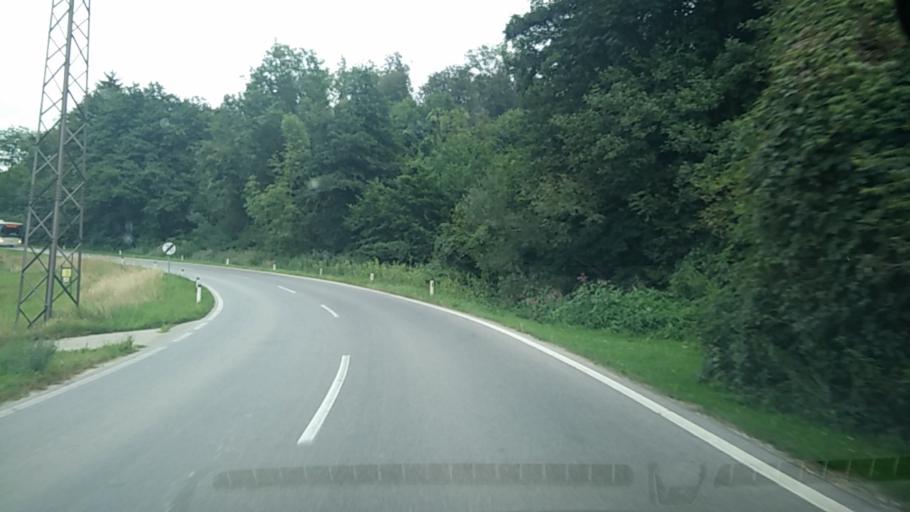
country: AT
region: Carinthia
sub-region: Politischer Bezirk Volkermarkt
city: Gallizien
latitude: 46.6184
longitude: 14.5500
